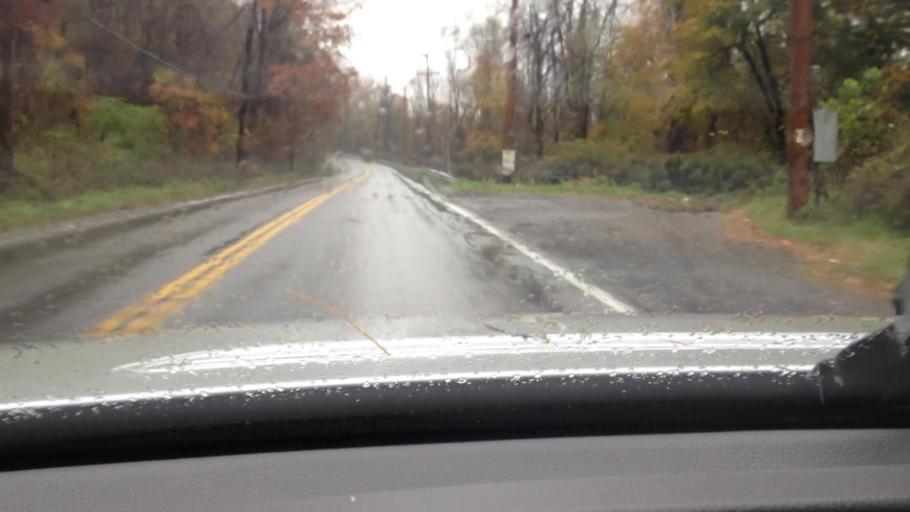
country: US
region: New York
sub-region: Dutchess County
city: Beacon
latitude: 41.4733
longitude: -73.9745
